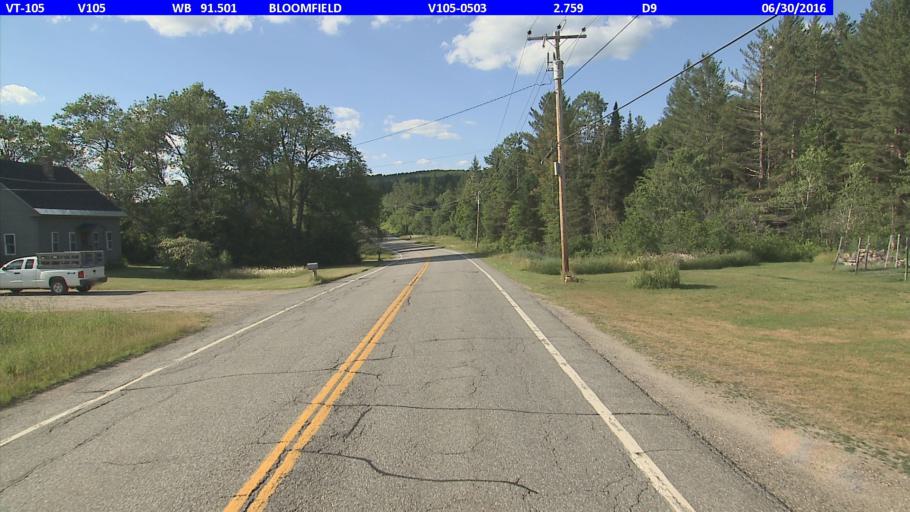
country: US
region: New Hampshire
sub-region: Coos County
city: Stratford
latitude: 44.7698
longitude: -71.6437
